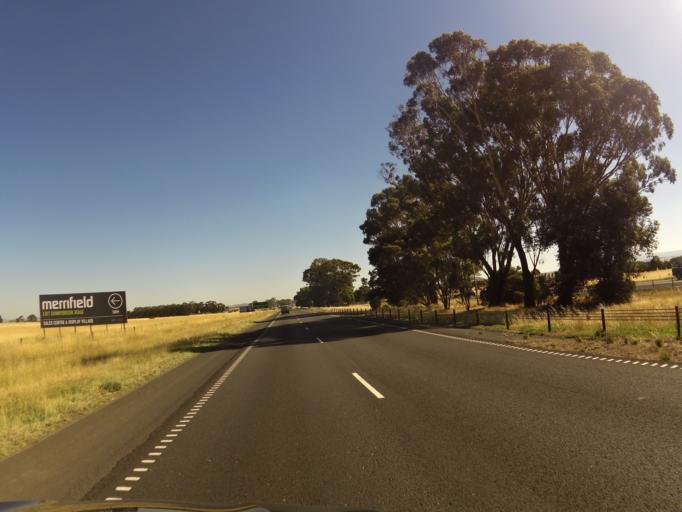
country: AU
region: Victoria
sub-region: Hume
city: Craigieburn
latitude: -37.5528
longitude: 144.9432
